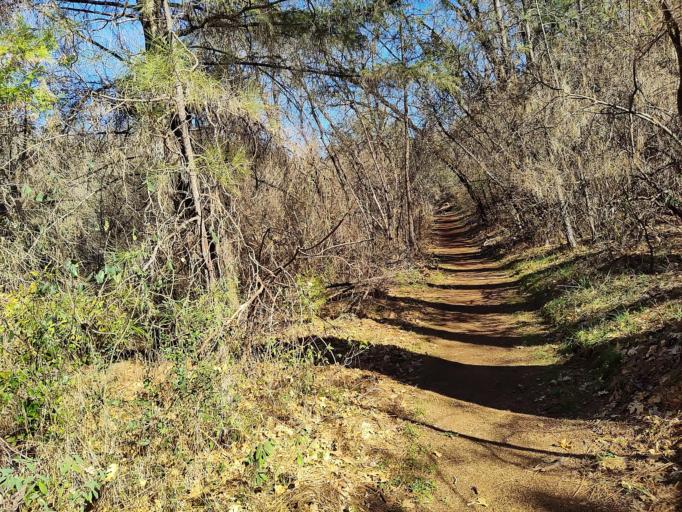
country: US
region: California
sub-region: Placer County
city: Meadow Vista
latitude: 39.0252
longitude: -120.9872
